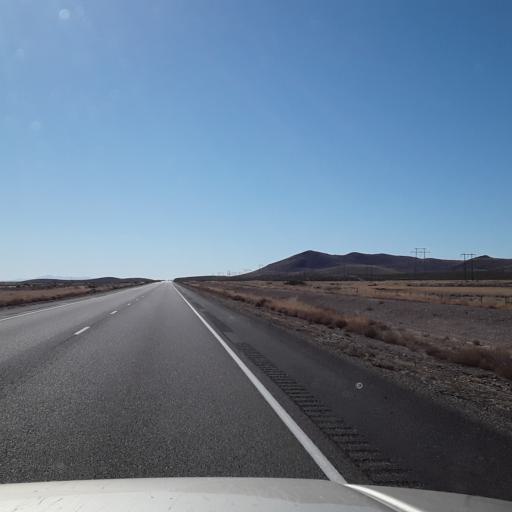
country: US
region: New Mexico
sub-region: Luna County
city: Deming
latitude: 32.3928
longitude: -107.5957
